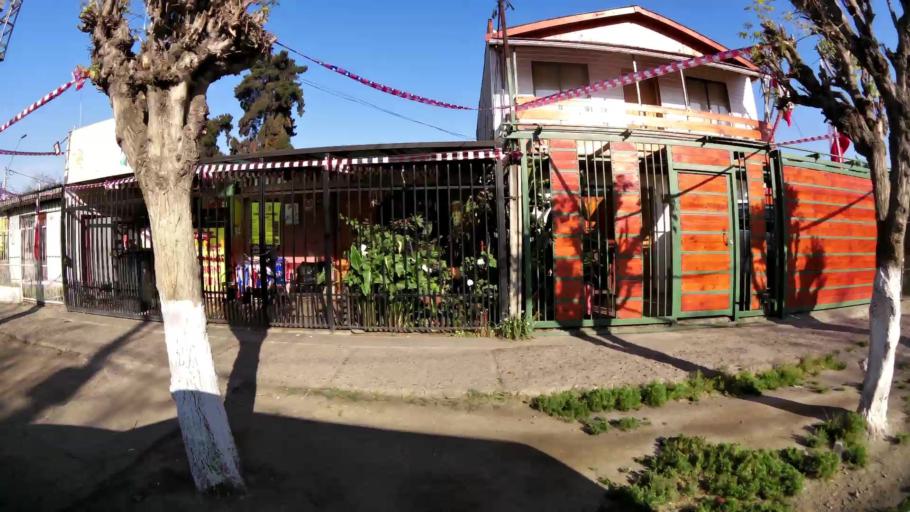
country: CL
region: Santiago Metropolitan
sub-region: Provincia de Santiago
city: Santiago
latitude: -33.3816
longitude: -70.6609
